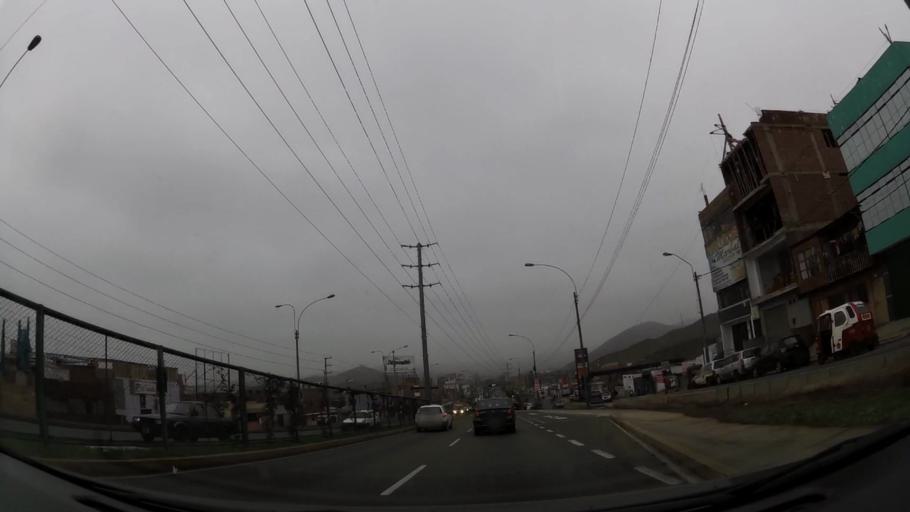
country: PE
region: Lima
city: Ventanilla
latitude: -11.8827
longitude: -77.1262
